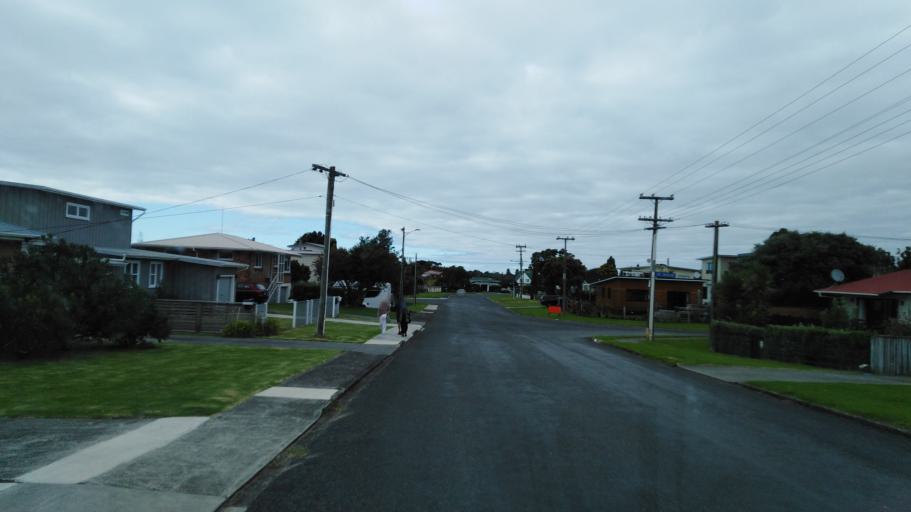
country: NZ
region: Bay of Plenty
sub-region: Western Bay of Plenty District
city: Waihi Beach
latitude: -37.4128
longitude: 175.9422
